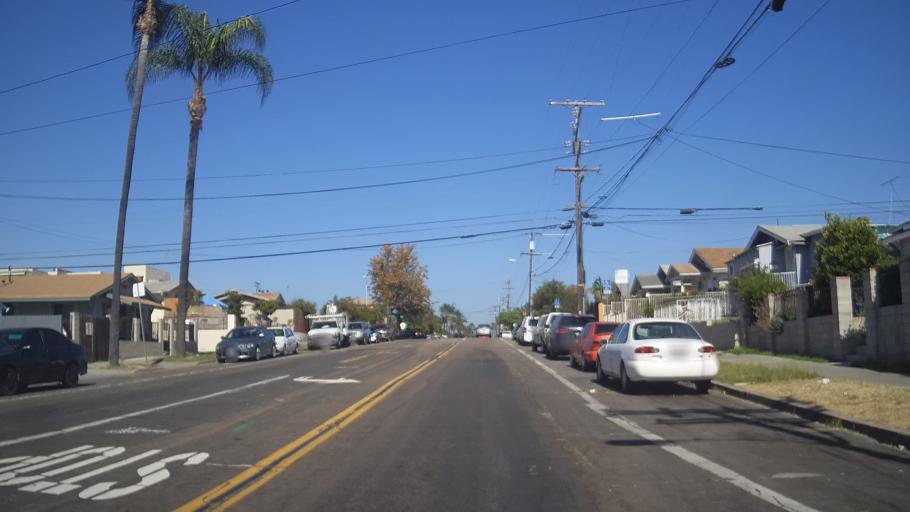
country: US
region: California
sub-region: San Diego County
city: San Diego
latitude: 32.7478
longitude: -117.1068
